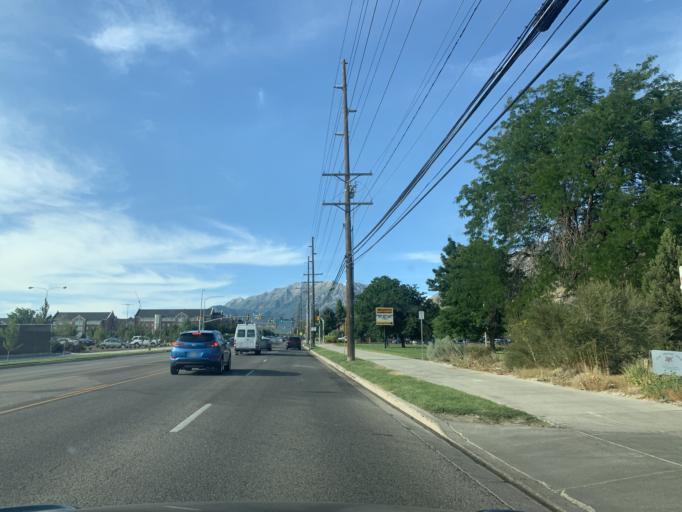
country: US
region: Utah
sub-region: Utah County
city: Provo
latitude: 40.2473
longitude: -111.6430
